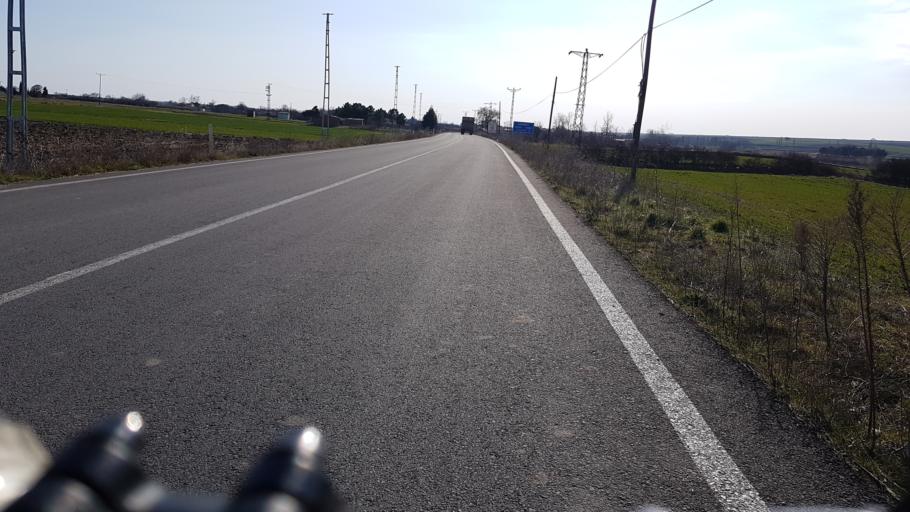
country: TR
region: Tekirdag
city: Velimese
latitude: 41.3503
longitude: 27.8395
